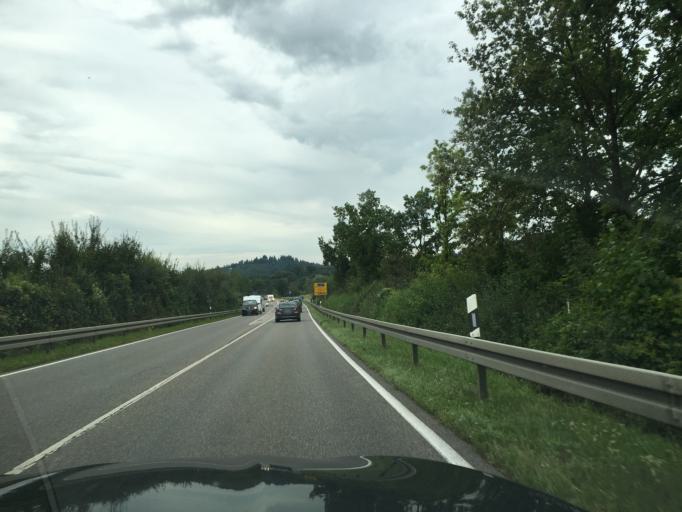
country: DE
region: Baden-Wuerttemberg
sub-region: Freiburg Region
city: Radolfzell am Bodensee
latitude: 47.7737
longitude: 8.9824
